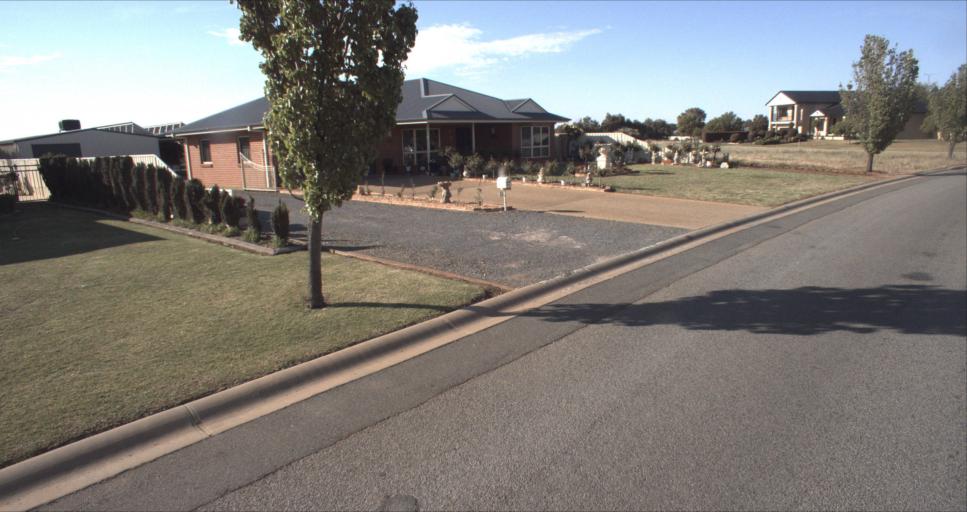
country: AU
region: New South Wales
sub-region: Leeton
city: Leeton
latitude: -34.5391
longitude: 146.4029
